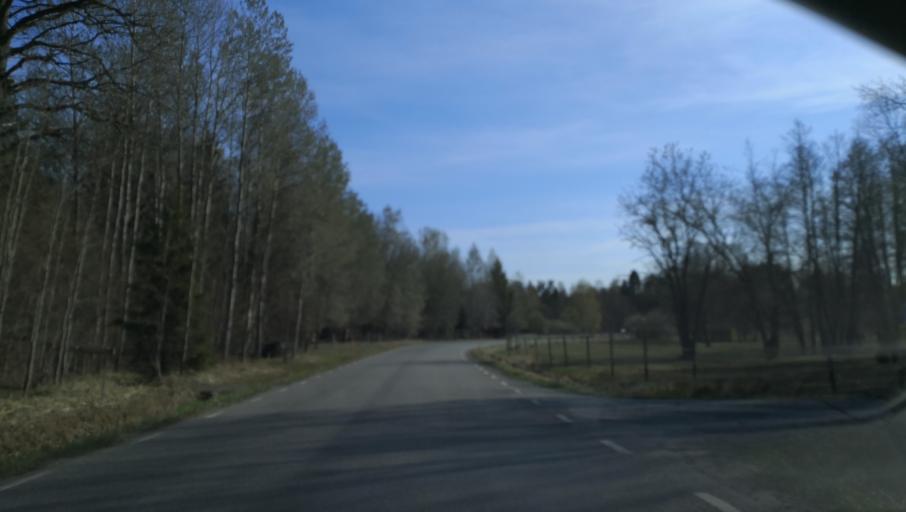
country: SE
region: Stockholm
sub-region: Varmdo Kommun
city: Holo
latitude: 59.2977
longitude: 18.6156
